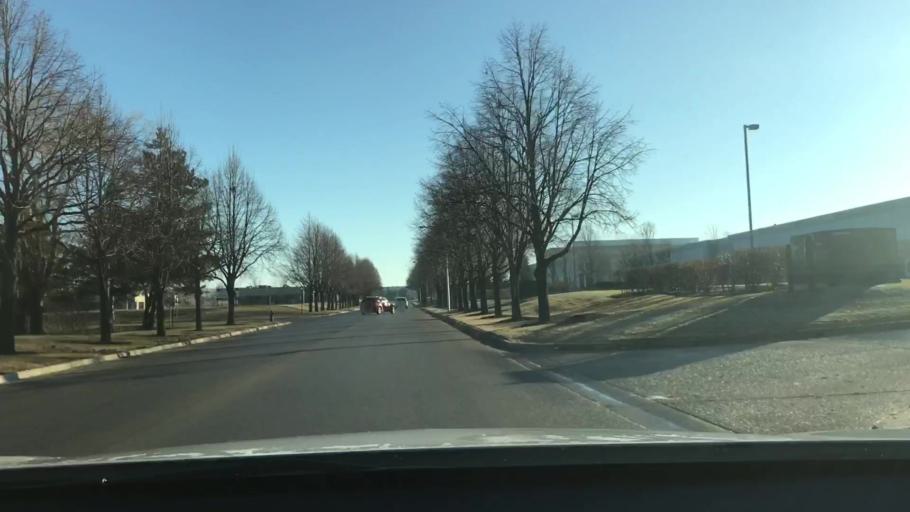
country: US
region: Illinois
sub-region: Kane County
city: Gilberts
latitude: 42.0753
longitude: -88.3412
